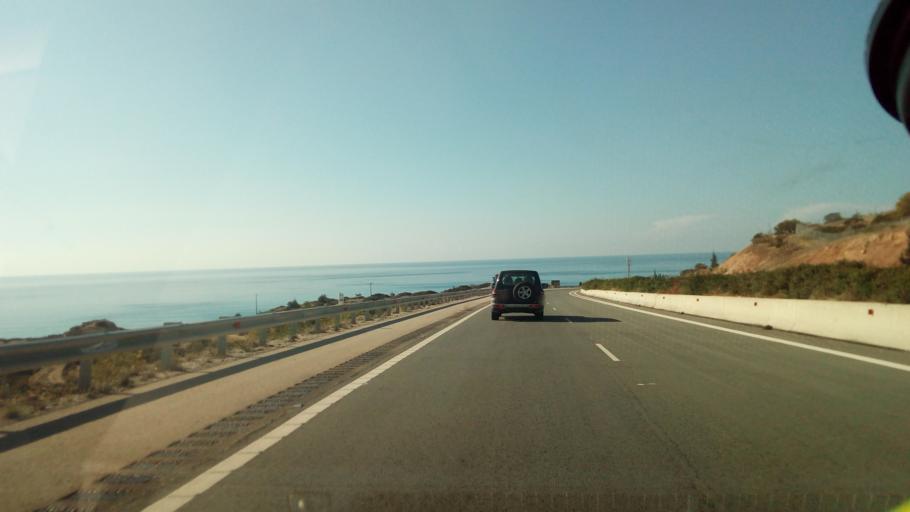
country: CY
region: Limassol
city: Pissouri
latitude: 34.6703
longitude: 32.6266
